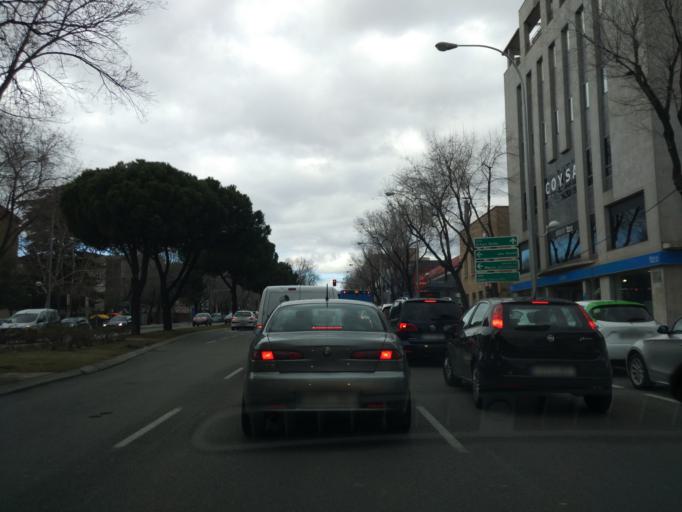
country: ES
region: Madrid
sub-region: Provincia de Madrid
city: San Blas
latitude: 40.4323
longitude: -3.6337
